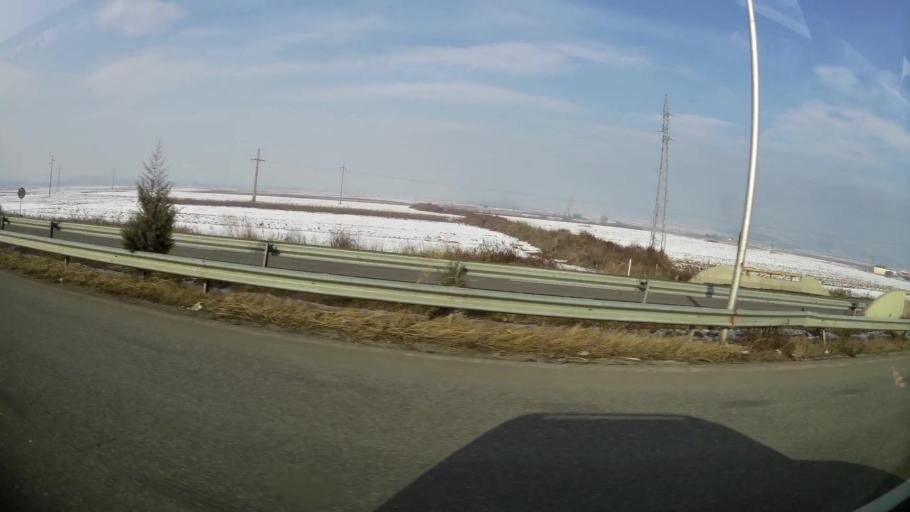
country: MK
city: Creshevo
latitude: 42.0309
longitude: 21.5075
